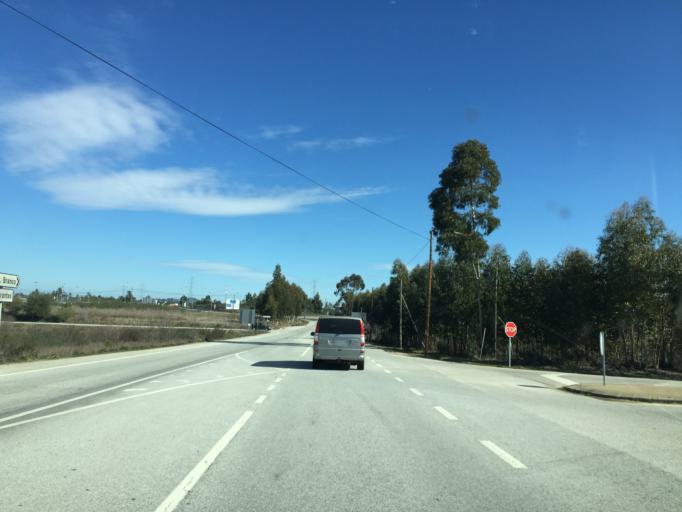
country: PT
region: Castelo Branco
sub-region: Castelo Branco
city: Castelo Branco
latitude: 39.7836
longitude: -7.5722
